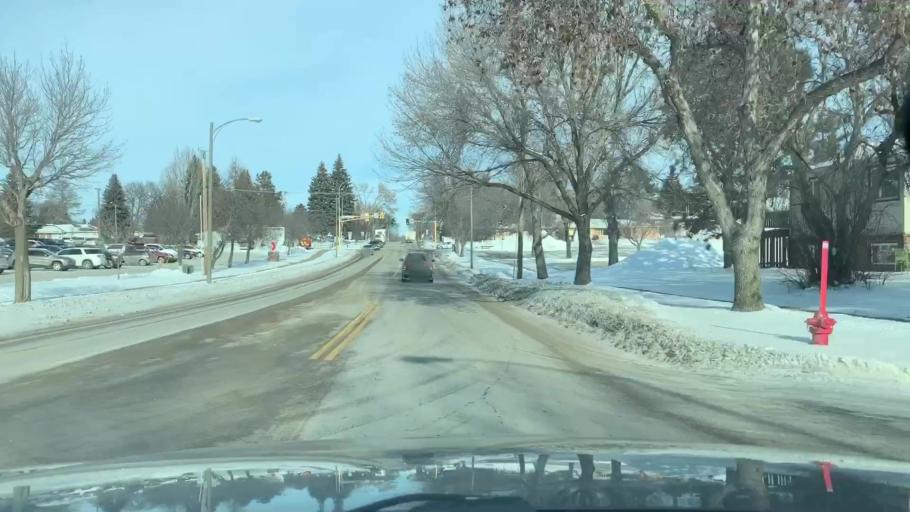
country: US
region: North Dakota
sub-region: Burleigh County
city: Bismarck
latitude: 46.8223
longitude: -100.7941
